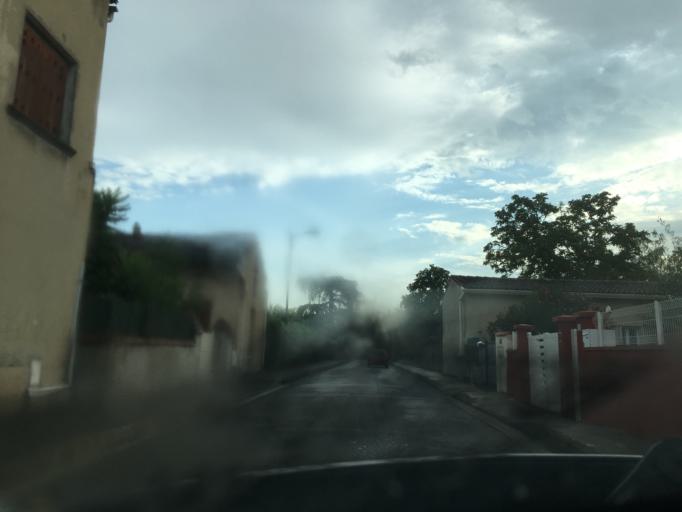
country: FR
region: Midi-Pyrenees
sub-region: Departement de la Haute-Garonne
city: Portet-sur-Garonne
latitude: 43.5583
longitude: 1.3815
